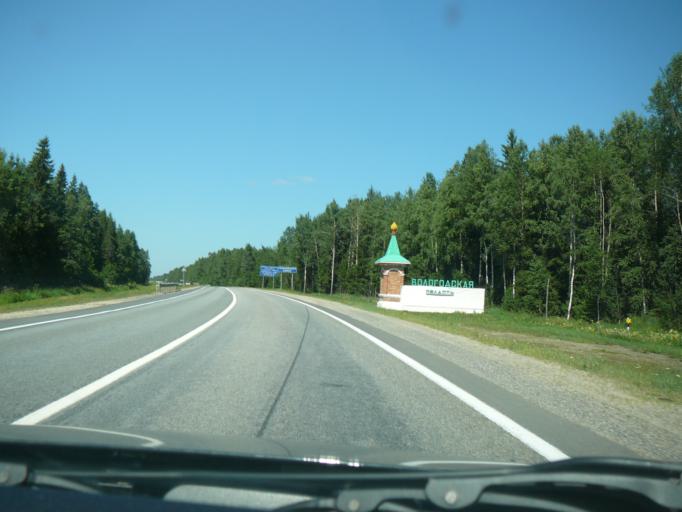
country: RU
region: Jaroslavl
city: Prechistoye
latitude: 58.5512
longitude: 40.3591
